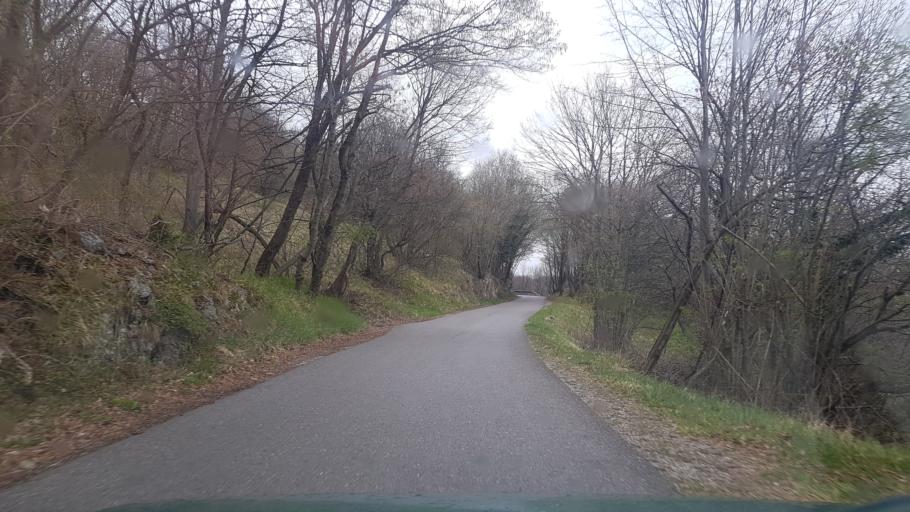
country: SI
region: Kanal
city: Deskle
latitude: 46.0675
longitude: 13.5695
